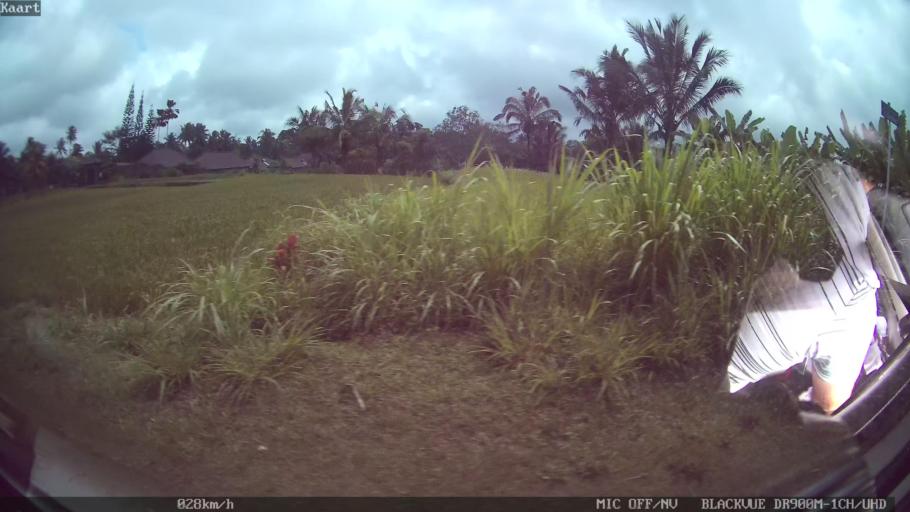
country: ID
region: Bali
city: Pemijian
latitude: -8.4361
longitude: 115.2264
